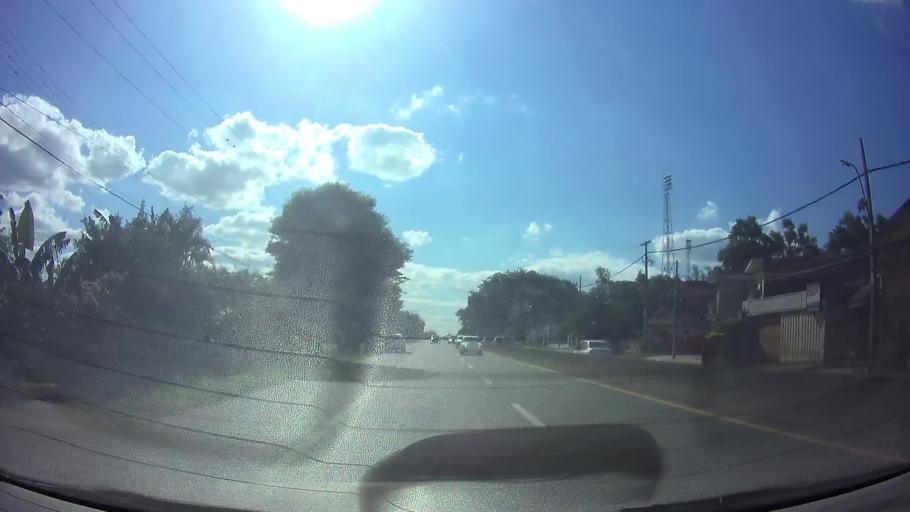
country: PY
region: Central
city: Itaugua
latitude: -25.3973
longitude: -57.3395
